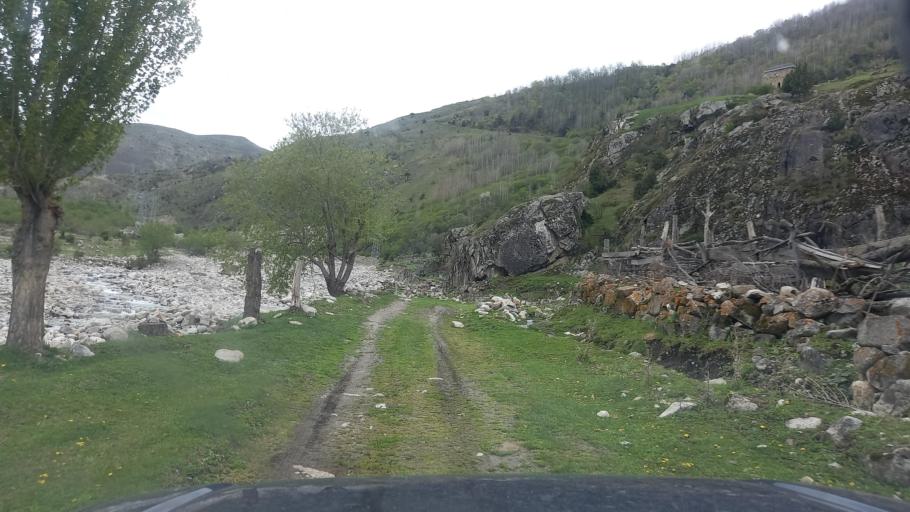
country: RU
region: Kabardino-Balkariya
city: Verkhnyaya Balkariya
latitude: 43.1023
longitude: 43.4372
